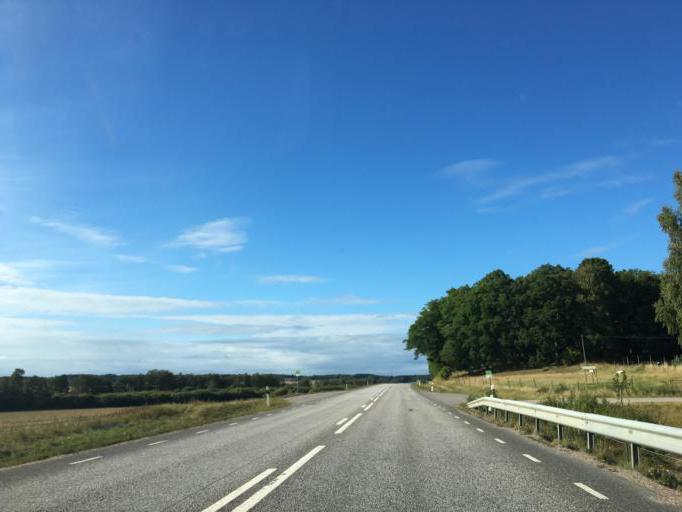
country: SE
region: Soedermanland
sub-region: Nykopings Kommun
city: Nykoping
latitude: 58.7845
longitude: 16.9632
